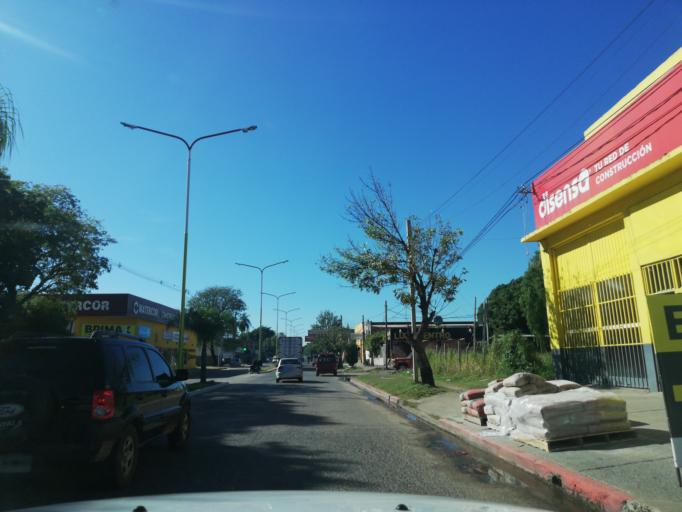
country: AR
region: Corrientes
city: Corrientes
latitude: -27.4754
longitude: -58.7961
